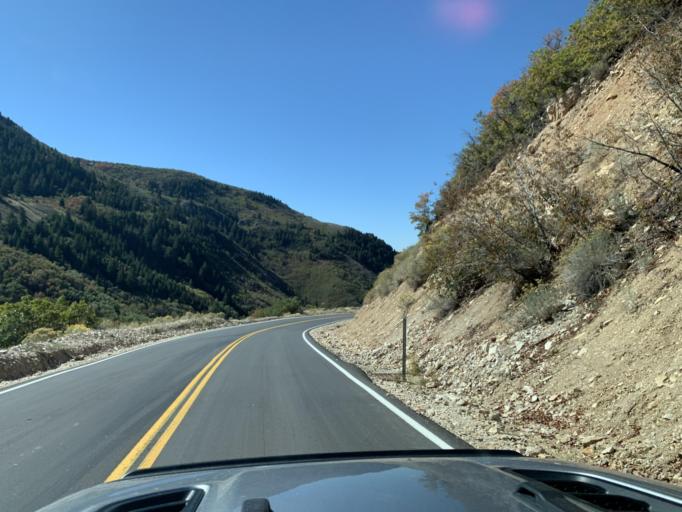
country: US
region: Utah
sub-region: Weber County
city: North Ogden
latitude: 41.3140
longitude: -111.9112
